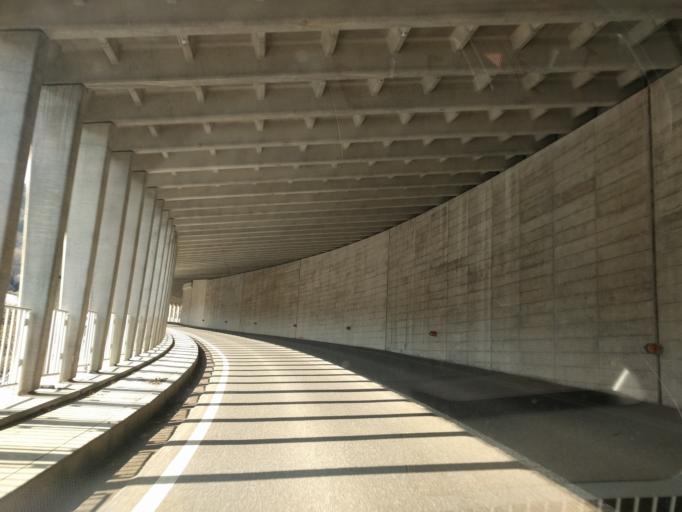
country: JP
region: Niigata
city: Muramatsu
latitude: 37.3264
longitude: 139.4670
